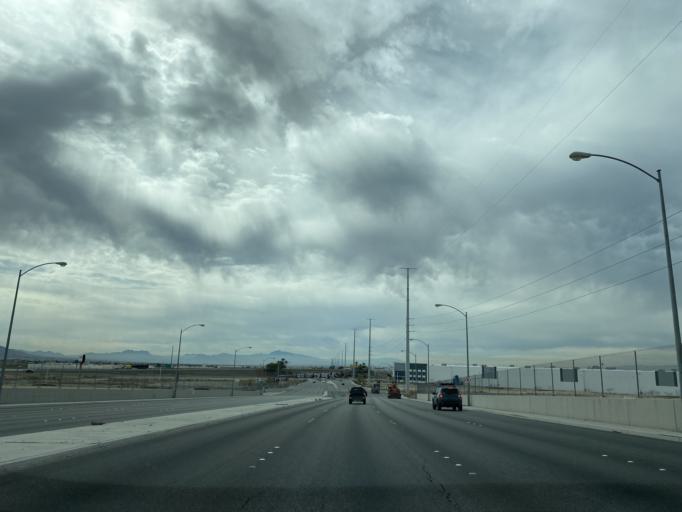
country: US
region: Nevada
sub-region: Clark County
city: Nellis Air Force Base
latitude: 36.2643
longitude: -115.0799
